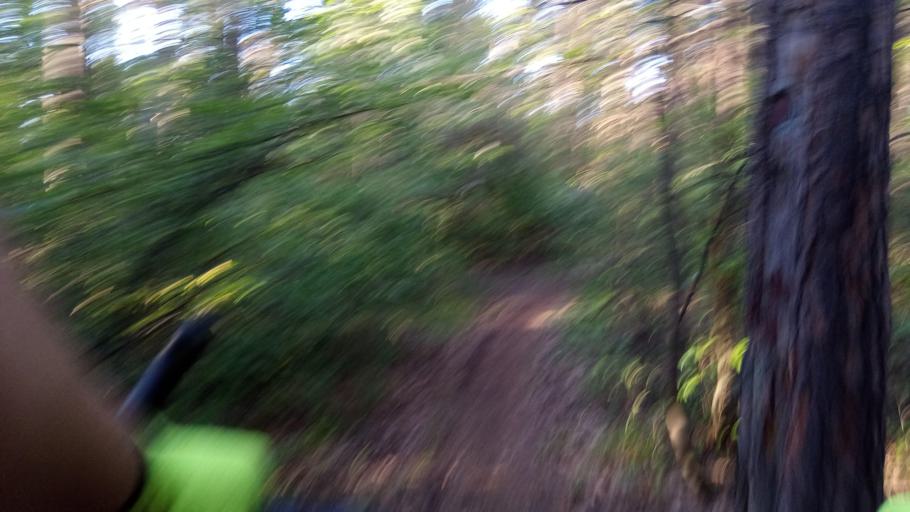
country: RU
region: Chelyabinsk
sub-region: Gorod Chelyabinsk
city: Chelyabinsk
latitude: 55.1363
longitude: 61.3302
